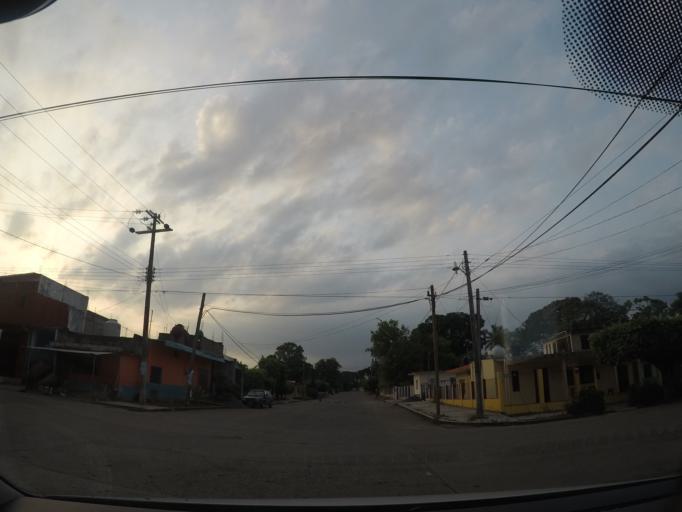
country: MX
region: Oaxaca
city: Matias Romero
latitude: 16.8746
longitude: -95.0359
